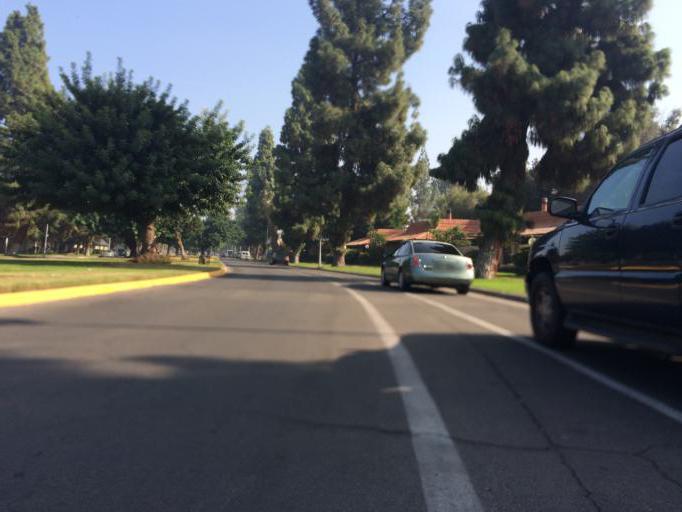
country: US
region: California
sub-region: Fresno County
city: Fresno
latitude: 36.7394
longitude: -119.7768
